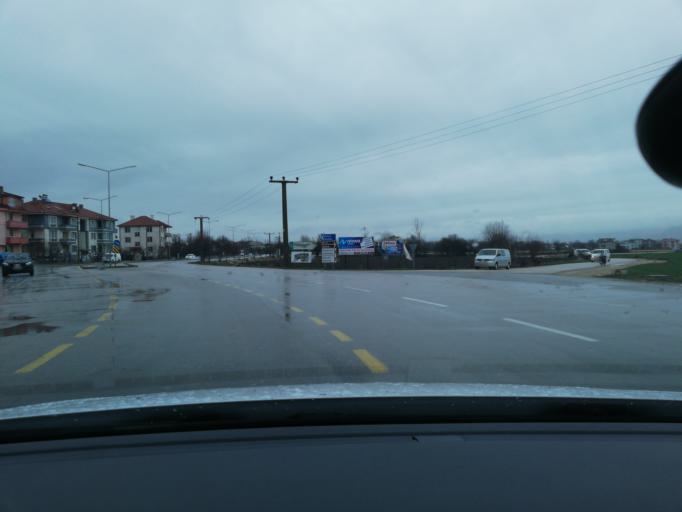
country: TR
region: Bolu
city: Bolu
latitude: 40.7270
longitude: 31.6227
